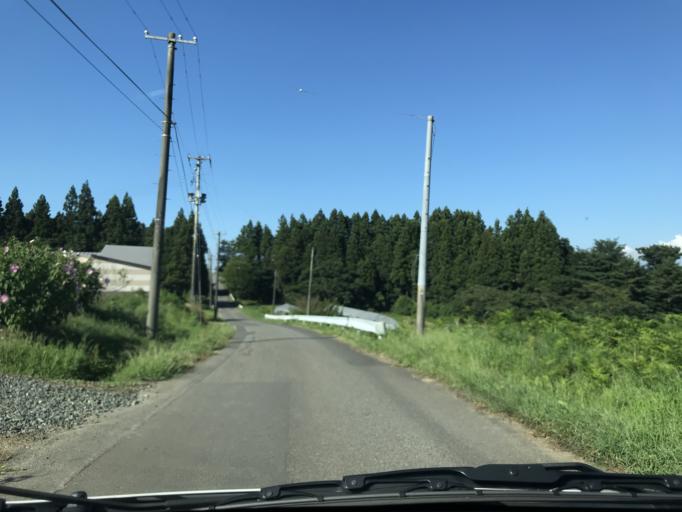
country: JP
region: Iwate
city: Mizusawa
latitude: 39.0704
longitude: 141.0461
